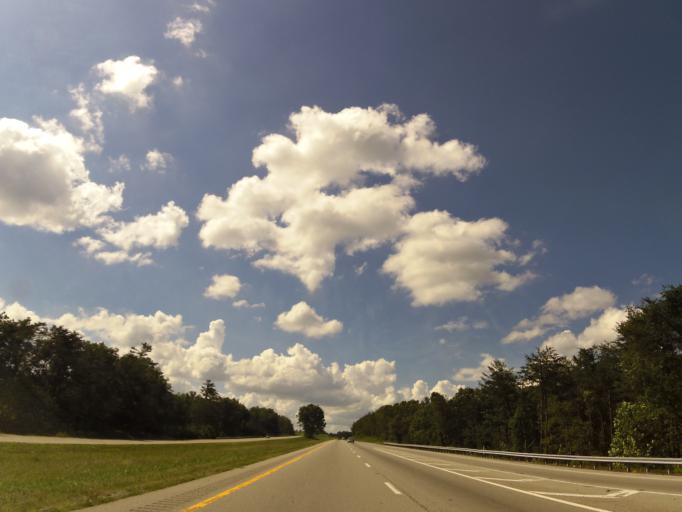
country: US
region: Tennessee
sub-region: Cumberland County
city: Fairfield Glade
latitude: 35.9278
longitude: -84.9173
